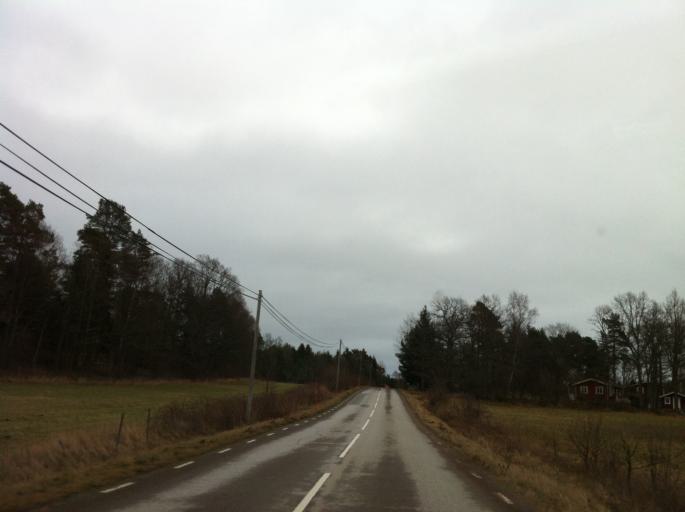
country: SE
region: Kalmar
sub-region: Vasterviks Kommun
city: Vaestervik
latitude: 57.8153
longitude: 16.5809
